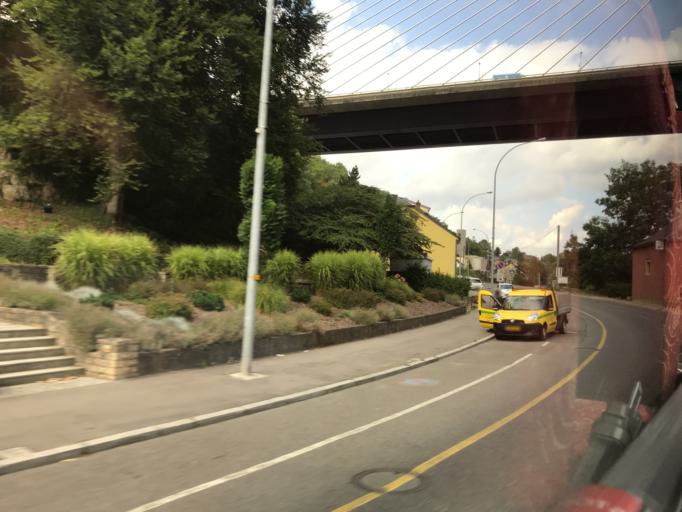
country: LU
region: Luxembourg
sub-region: Canton de Luxembourg
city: Hesperange
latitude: 49.5783
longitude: 6.1537
